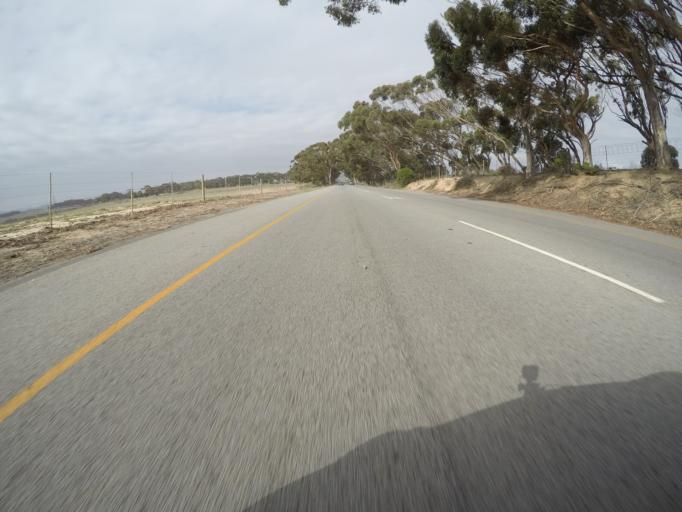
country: ZA
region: Western Cape
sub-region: City of Cape Town
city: Sunset Beach
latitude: -33.7233
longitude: 18.5017
